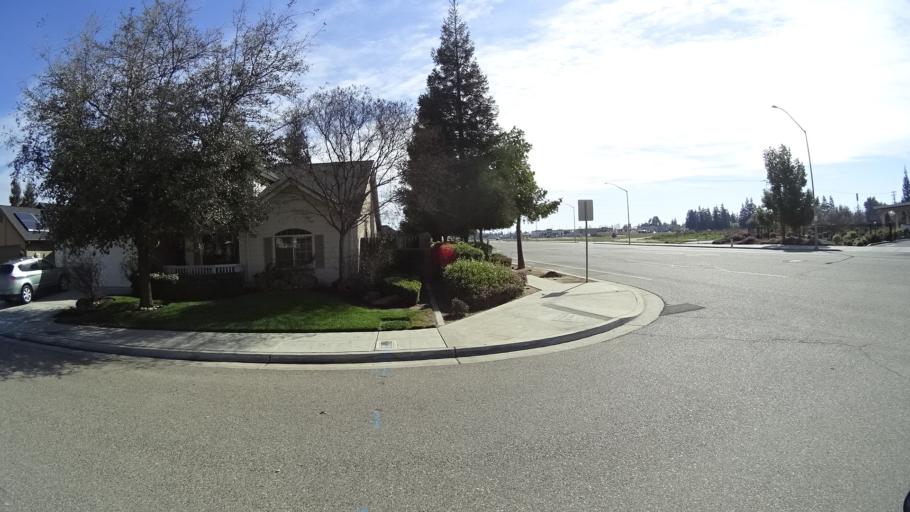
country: US
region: California
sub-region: Fresno County
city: West Park
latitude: 36.8388
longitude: -119.8752
